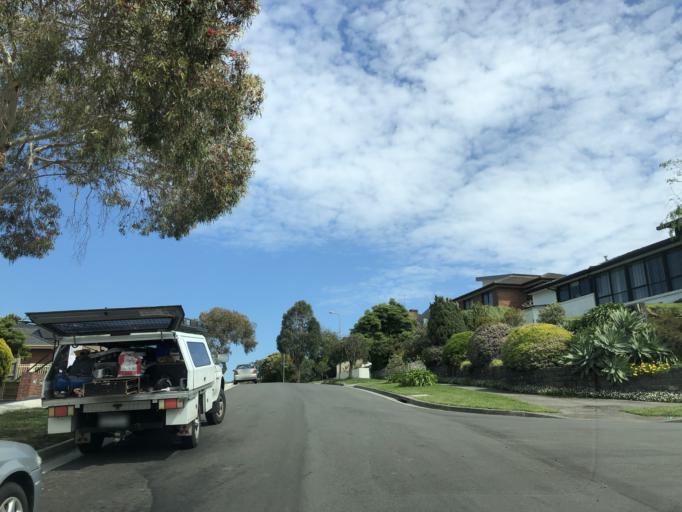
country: AU
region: Victoria
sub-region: Casey
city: Endeavour Hills
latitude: -37.9852
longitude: 145.2588
